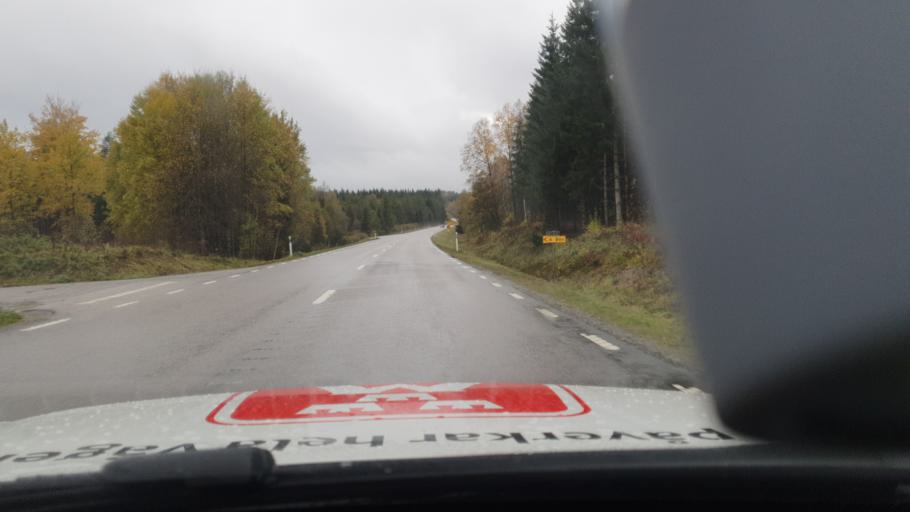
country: SE
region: Vaestra Goetaland
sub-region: Dals-Ed Kommun
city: Ed
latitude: 58.8946
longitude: 11.9286
